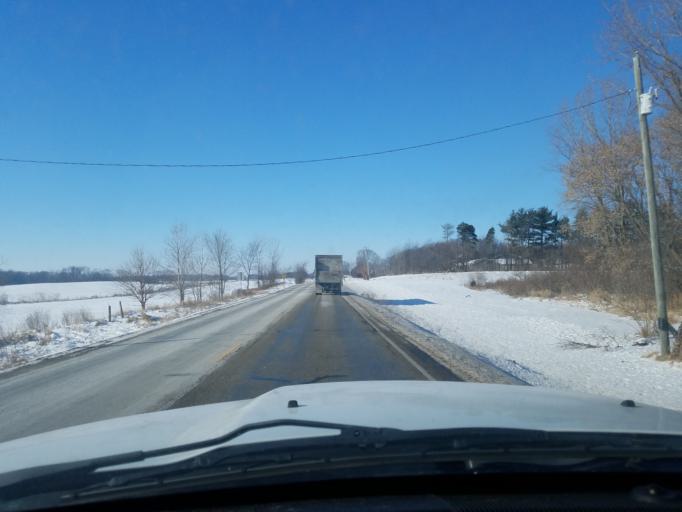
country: US
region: Indiana
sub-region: Noble County
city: Kendallville
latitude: 41.3955
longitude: -85.3331
